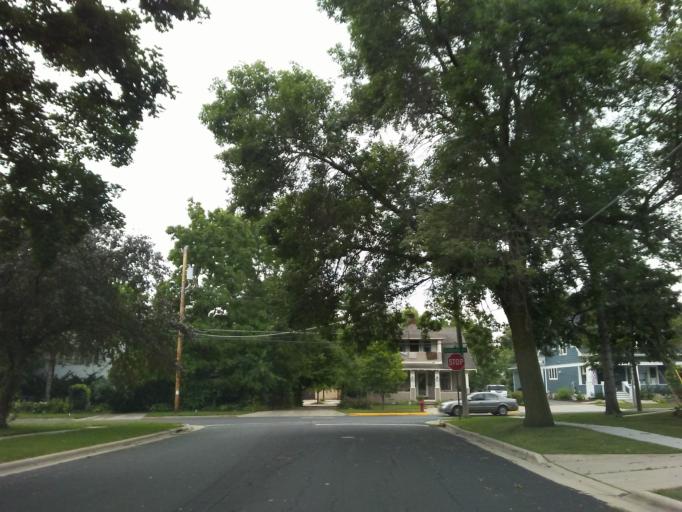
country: US
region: Wisconsin
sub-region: Dane County
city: Middleton
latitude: 43.0954
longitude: -89.5067
